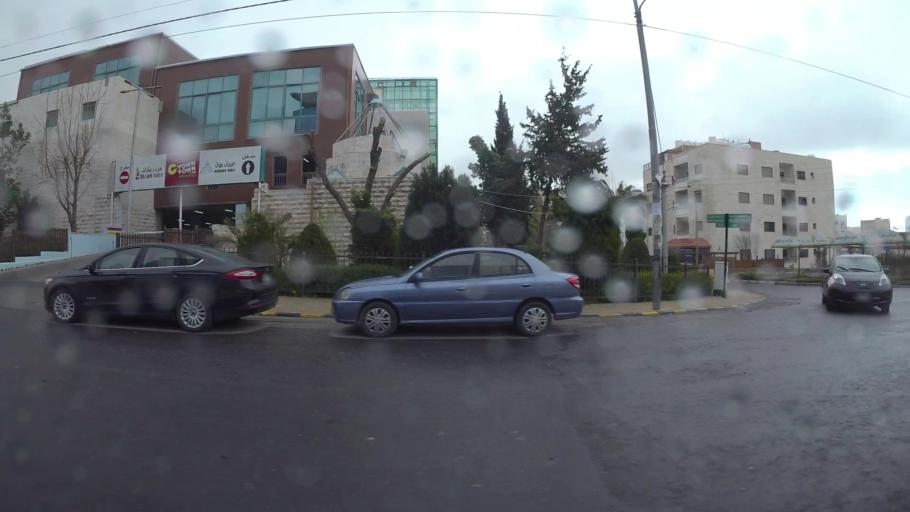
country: JO
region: Amman
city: Al Jubayhah
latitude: 31.9899
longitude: 35.8652
